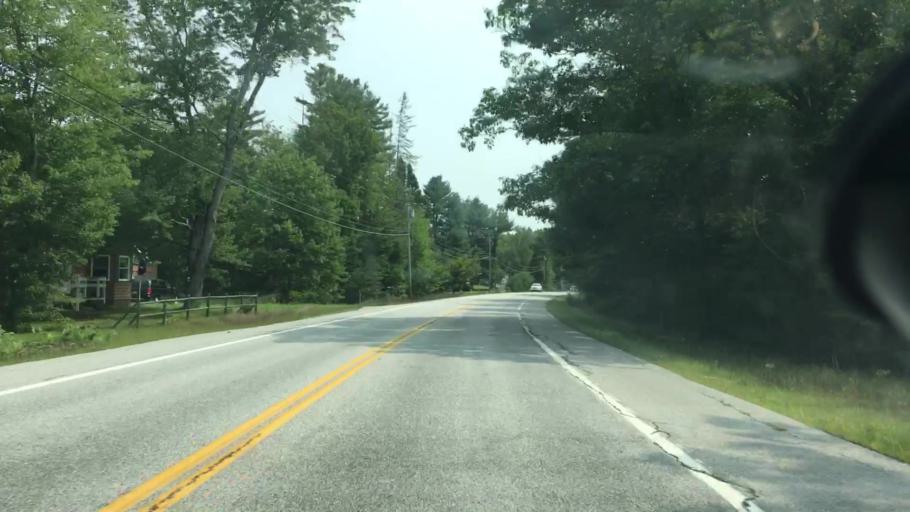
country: US
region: Maine
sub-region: Androscoggin County
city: Livermore Falls
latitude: 44.4475
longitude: -70.1578
